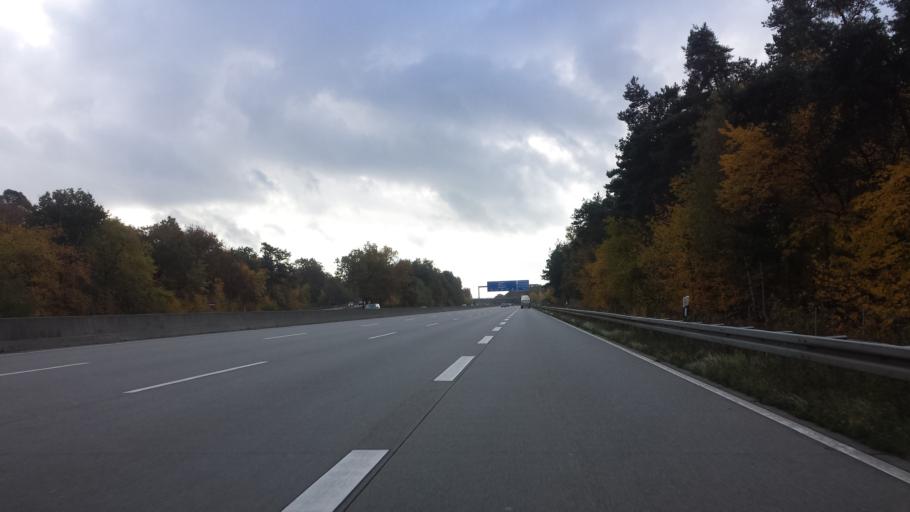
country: DE
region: Hesse
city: Viernheim
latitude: 49.5655
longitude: 8.5587
